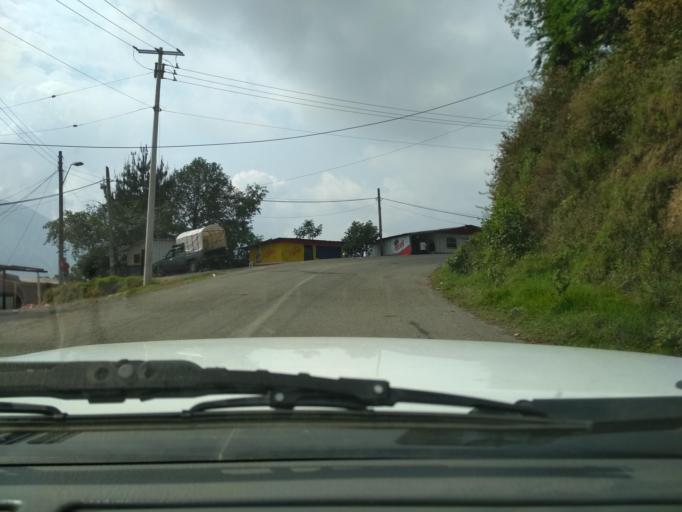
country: MX
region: Veracruz
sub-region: Camerino Z. Mendoza
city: Necoxtla
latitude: 18.7709
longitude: -97.1517
